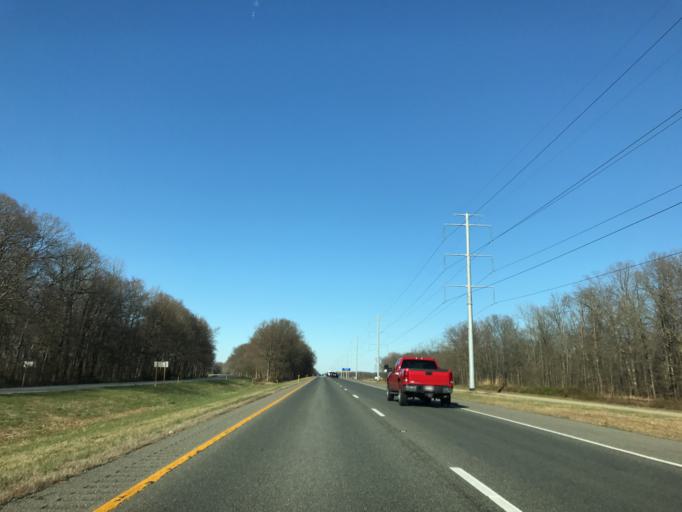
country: US
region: Maryland
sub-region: Queen Anne's County
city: Centreville
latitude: 39.0710
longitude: -75.9850
